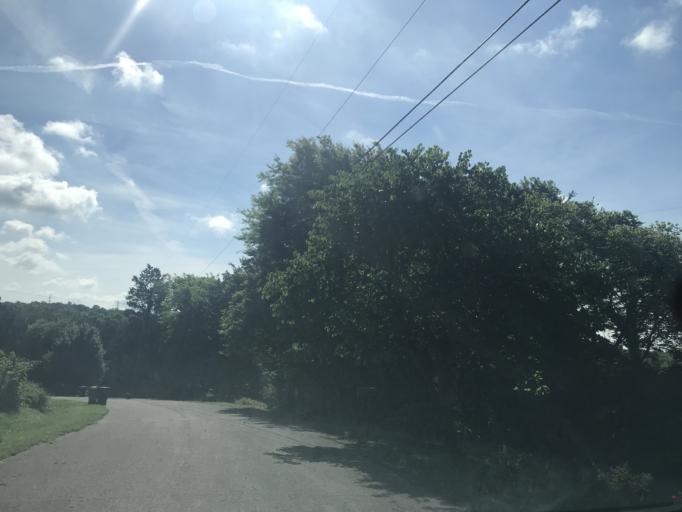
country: US
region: Tennessee
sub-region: Davidson County
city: Nashville
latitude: 36.1983
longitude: -86.8484
